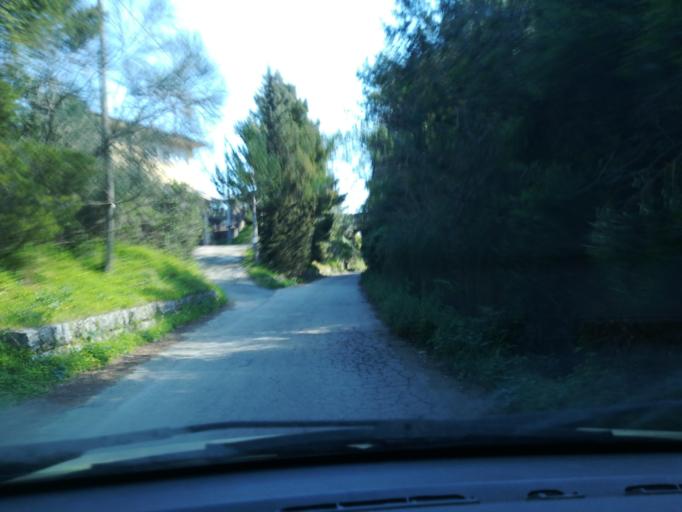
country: IT
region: Sicily
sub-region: Palermo
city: Cannizzaro-Favara
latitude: 38.0463
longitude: 13.2638
